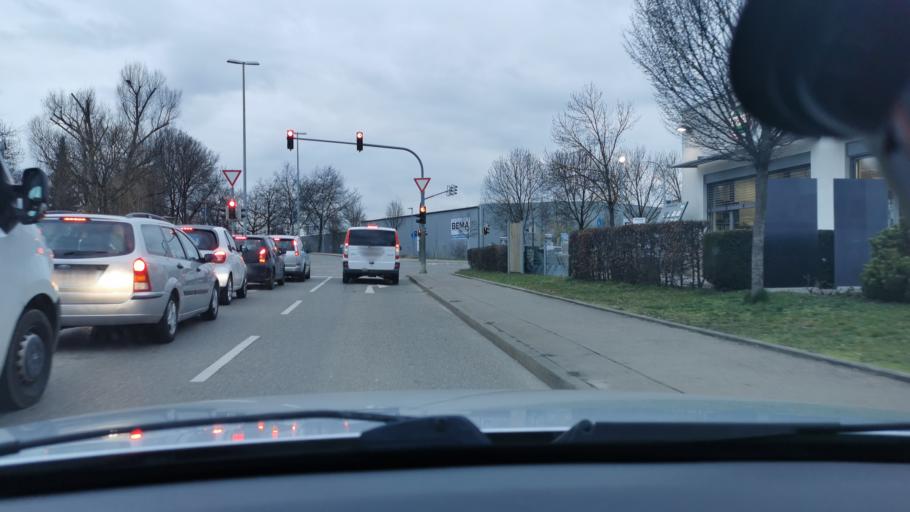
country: DE
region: Baden-Wuerttemberg
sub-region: Regierungsbezirk Stuttgart
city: Kirchheim unter Teck
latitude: 48.6492
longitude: 9.4317
